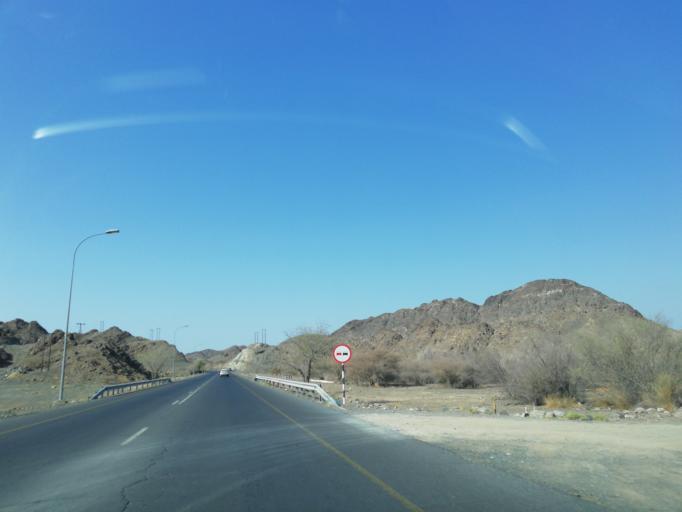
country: OM
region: Ash Sharqiyah
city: Ibra'
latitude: 22.8231
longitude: 58.1682
